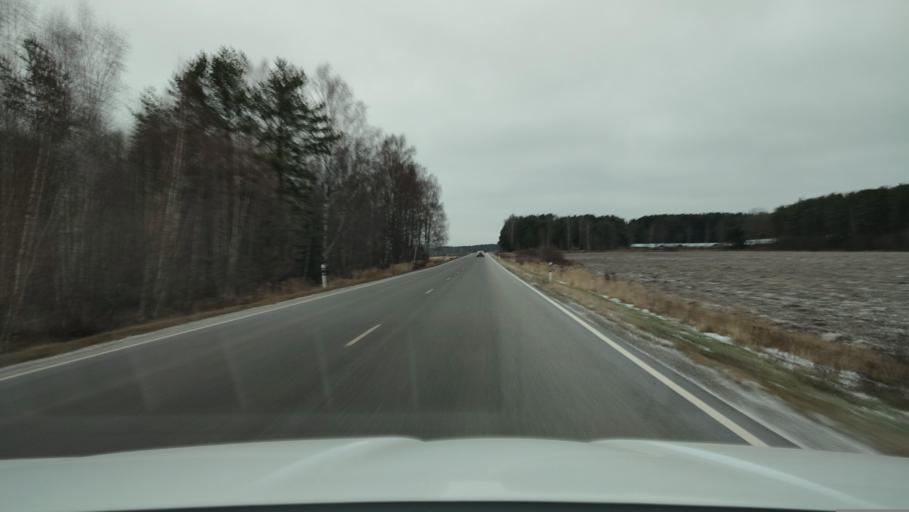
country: FI
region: Ostrobothnia
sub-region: Sydosterbotten
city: Naerpes
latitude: 62.5344
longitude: 21.4640
